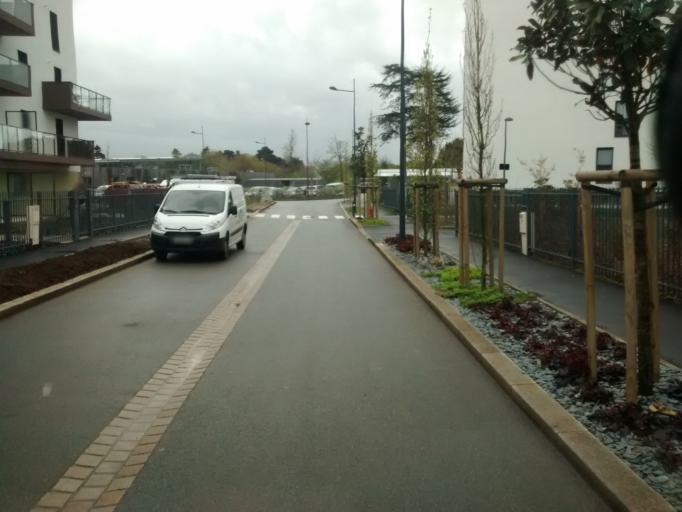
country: FR
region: Brittany
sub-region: Departement du Morbihan
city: Hennebont
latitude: 47.8061
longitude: -3.2709
